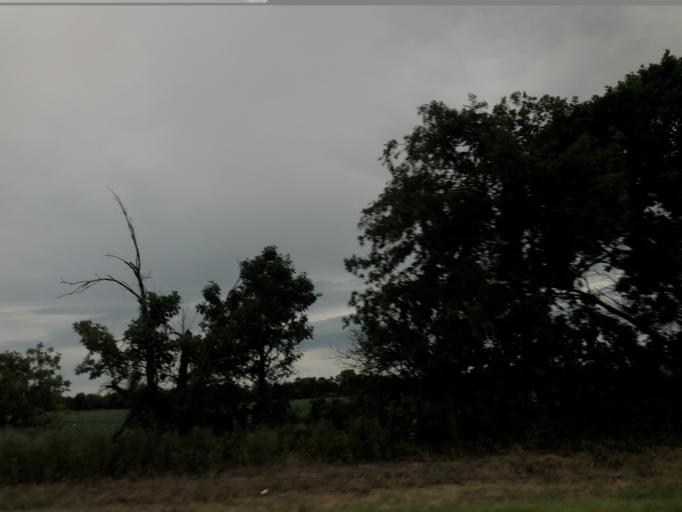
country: US
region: Kansas
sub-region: Reno County
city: Hutchinson
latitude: 38.1147
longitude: -97.9468
